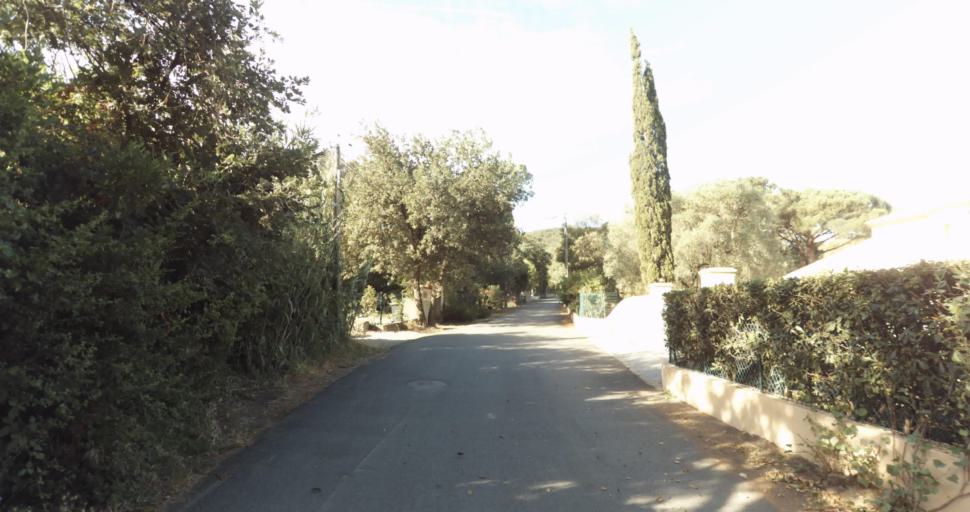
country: FR
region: Provence-Alpes-Cote d'Azur
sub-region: Departement du Var
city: Saint-Tropez
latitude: 43.2586
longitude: 6.6281
